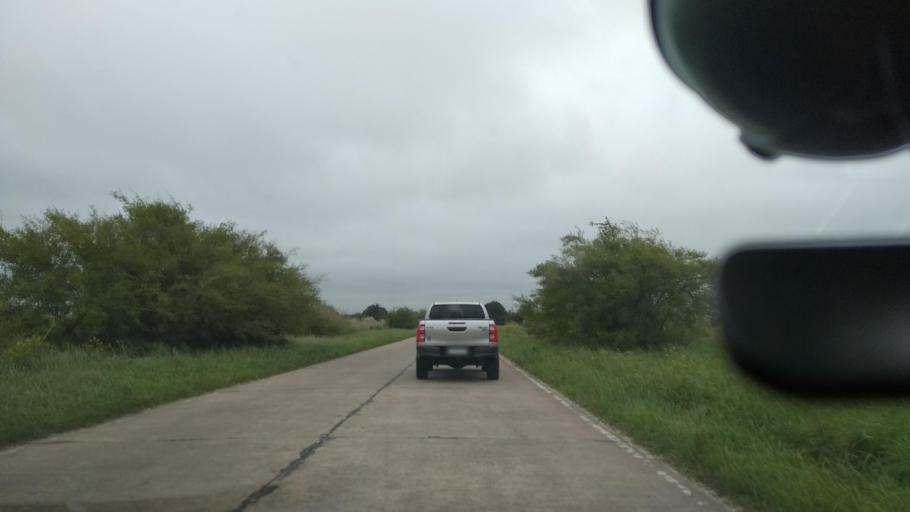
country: AR
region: Buenos Aires
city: Veronica
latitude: -35.5386
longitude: -57.3178
